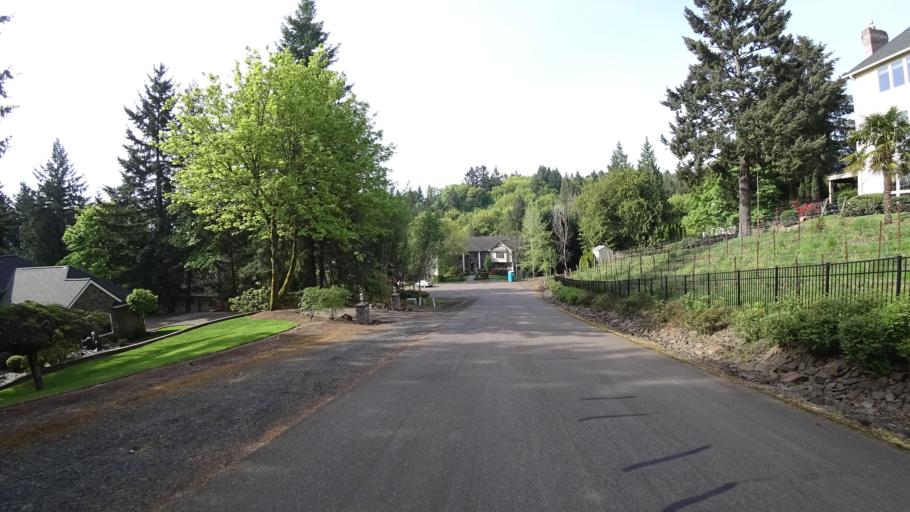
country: US
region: Oregon
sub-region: Washington County
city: Aloha
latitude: 45.4446
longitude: -122.8480
